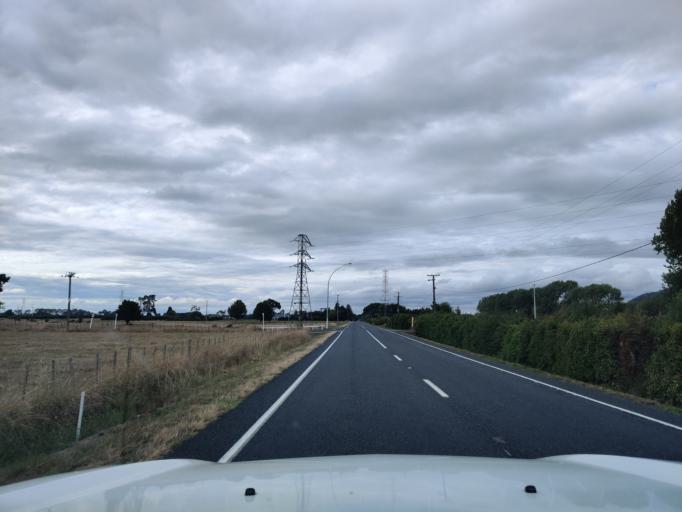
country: NZ
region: Waikato
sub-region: Waipa District
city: Cambridge
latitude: -37.8463
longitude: 175.4536
